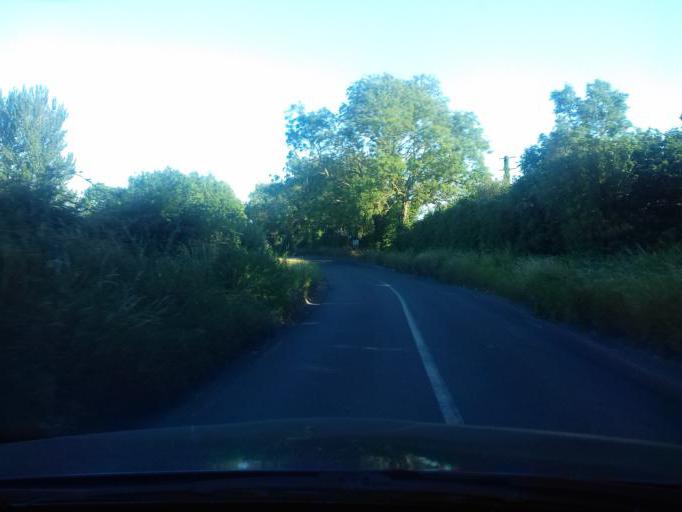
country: IE
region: Leinster
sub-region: Dublin City
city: Finglas
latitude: 53.4413
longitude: -6.2994
